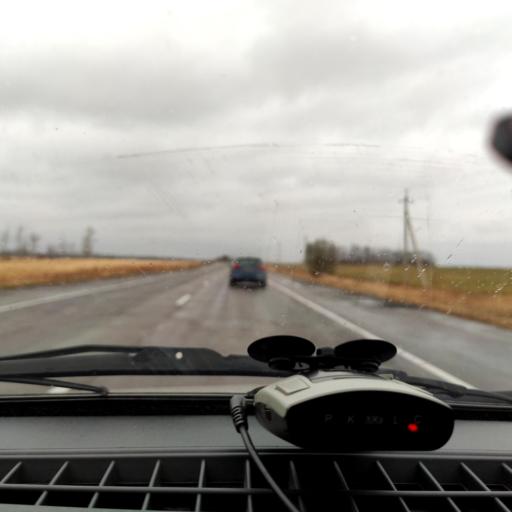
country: RU
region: Voronezj
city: Strelitsa
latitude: 51.5591
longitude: 38.9729
